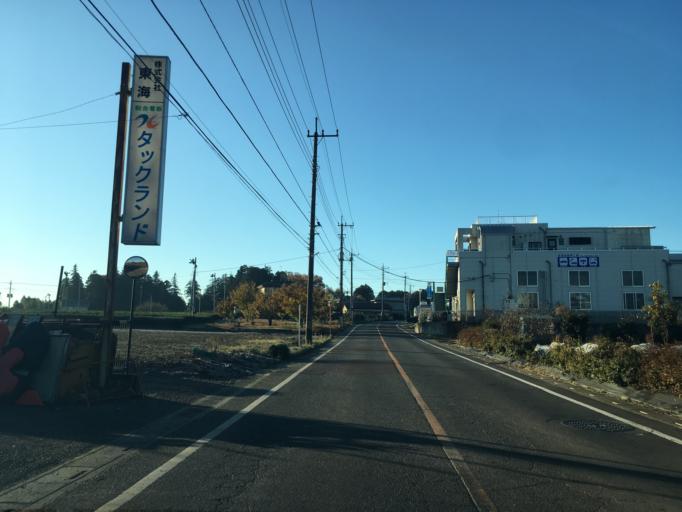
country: JP
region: Saitama
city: Tokorozawa
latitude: 35.7946
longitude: 139.4159
